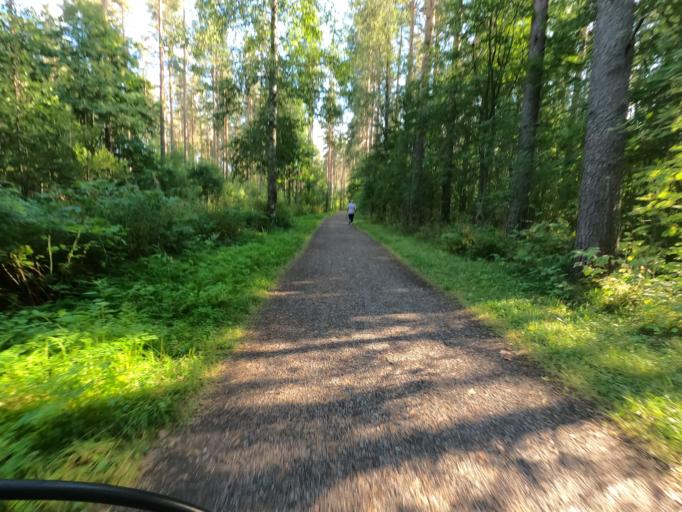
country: FI
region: North Karelia
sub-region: Joensuu
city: Joensuu
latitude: 62.6156
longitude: 29.7525
